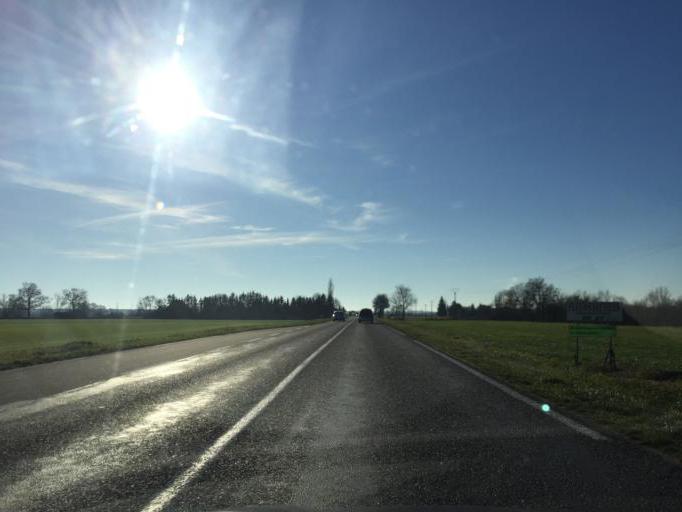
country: FR
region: Auvergne
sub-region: Departement de l'Allier
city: Saint-Pourcain-sur-Sioule
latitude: 46.2691
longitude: 3.2899
